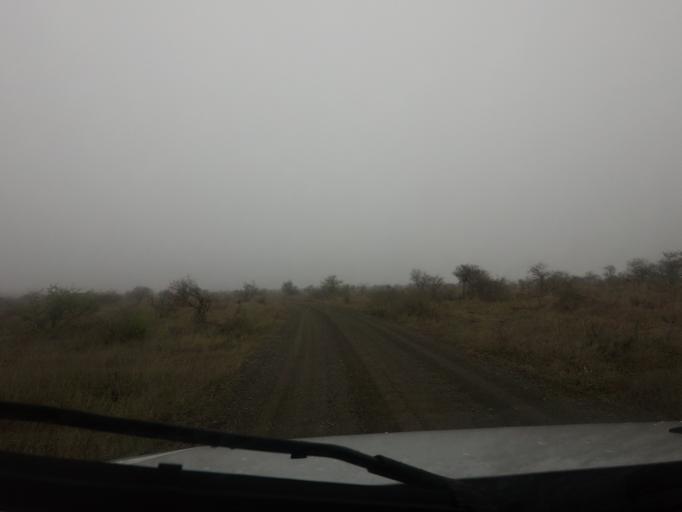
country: ZA
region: Limpopo
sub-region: Mopani District Municipality
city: Phalaborwa
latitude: -24.2600
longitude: 31.6655
